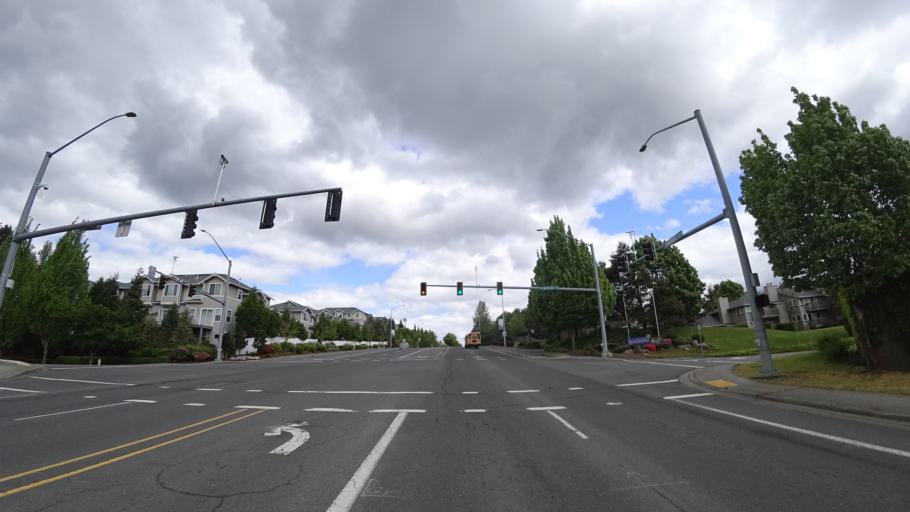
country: US
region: Oregon
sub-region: Washington County
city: Beaverton
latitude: 45.4554
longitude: -122.8261
